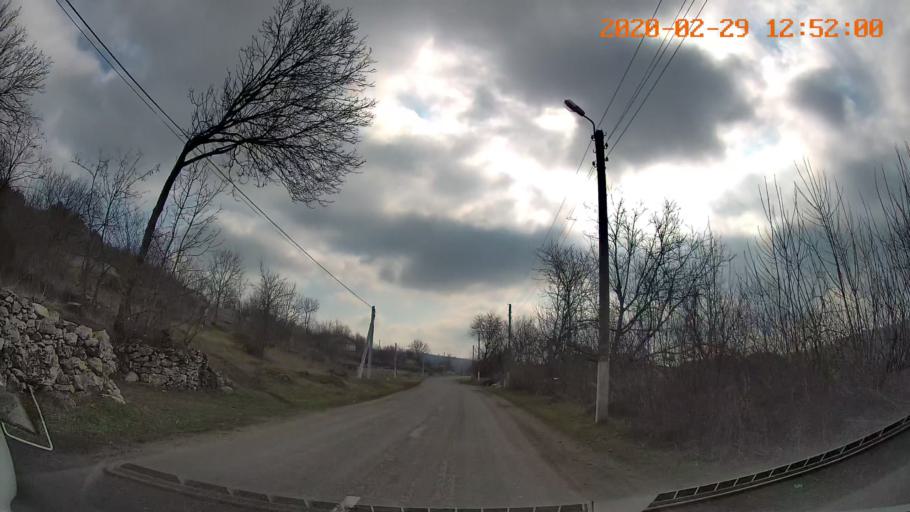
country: MD
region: Telenesti
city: Camenca
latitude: 48.1153
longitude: 28.7319
